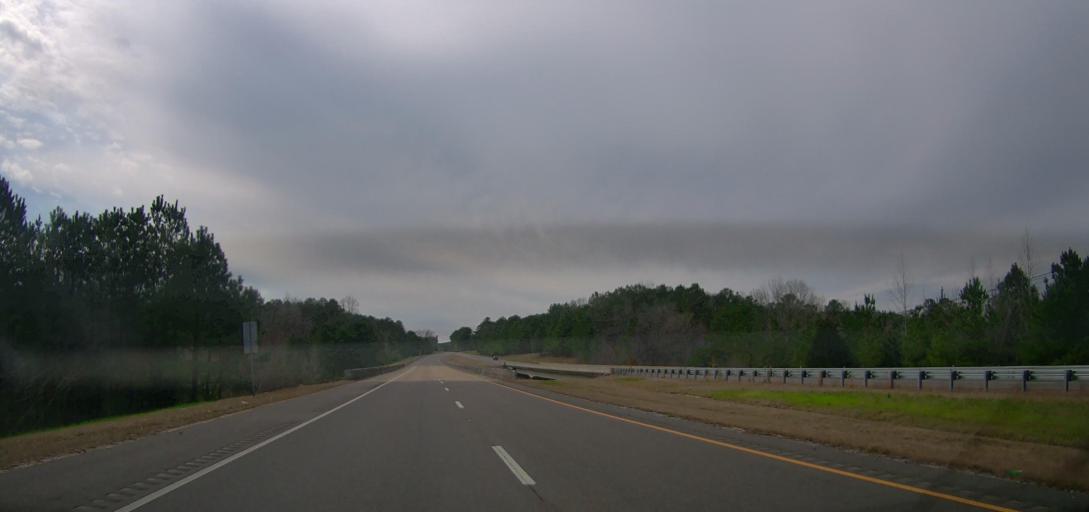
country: US
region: Alabama
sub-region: Walker County
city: Carbon Hill
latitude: 33.8716
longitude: -87.4474
